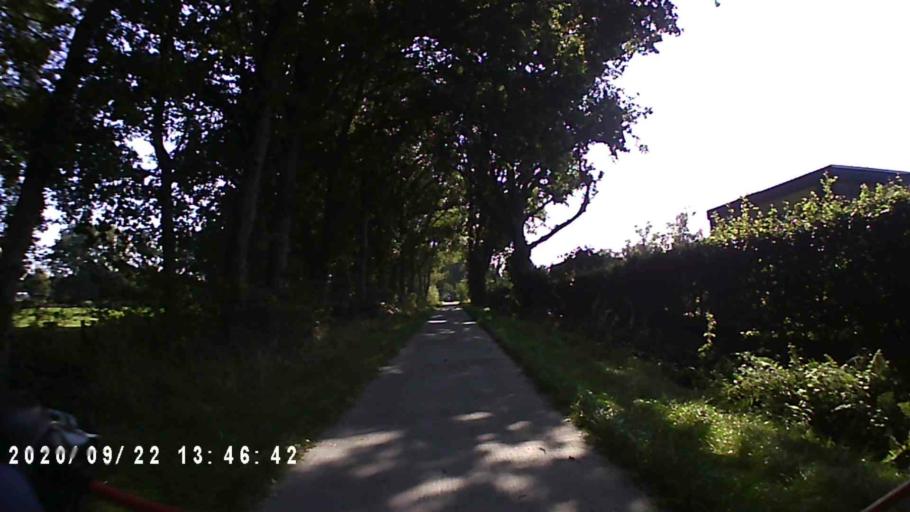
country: NL
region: Groningen
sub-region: Gemeente Leek
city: Leek
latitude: 53.1426
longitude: 6.4093
